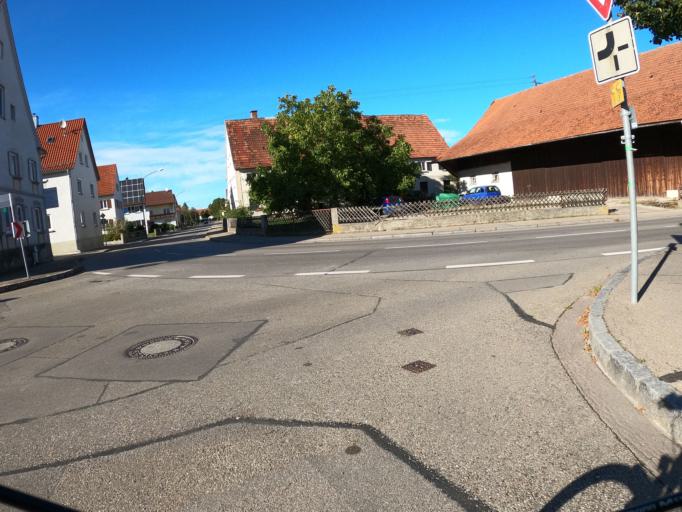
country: DE
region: Bavaria
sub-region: Swabia
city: Nersingen
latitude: 48.4149
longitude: 10.1364
